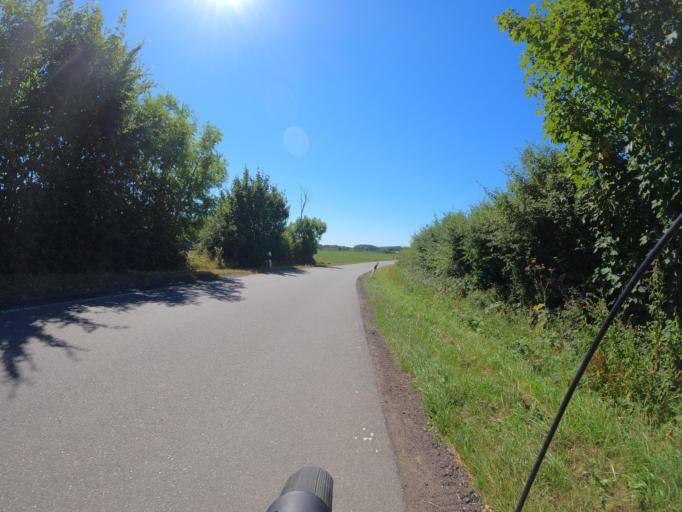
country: DE
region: Schleswig-Holstein
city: Quern
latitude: 54.7939
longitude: 9.7337
